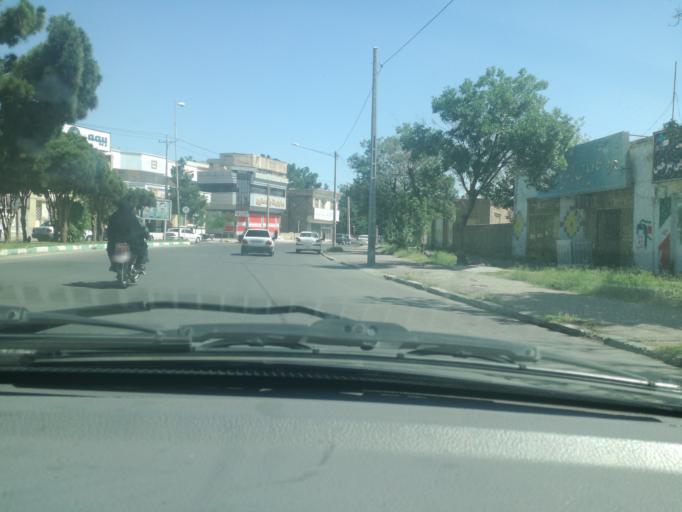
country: IR
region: Razavi Khorasan
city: Sarakhs
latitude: 36.5338
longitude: 61.1618
